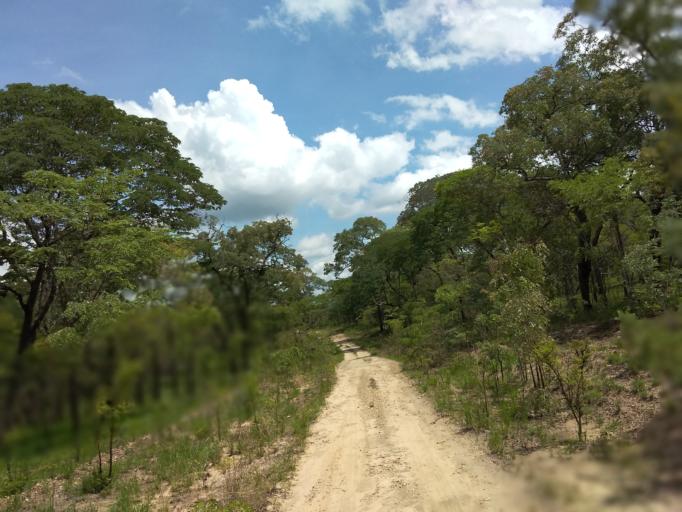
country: ZM
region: Central
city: Mkushi
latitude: -14.0776
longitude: 29.9678
